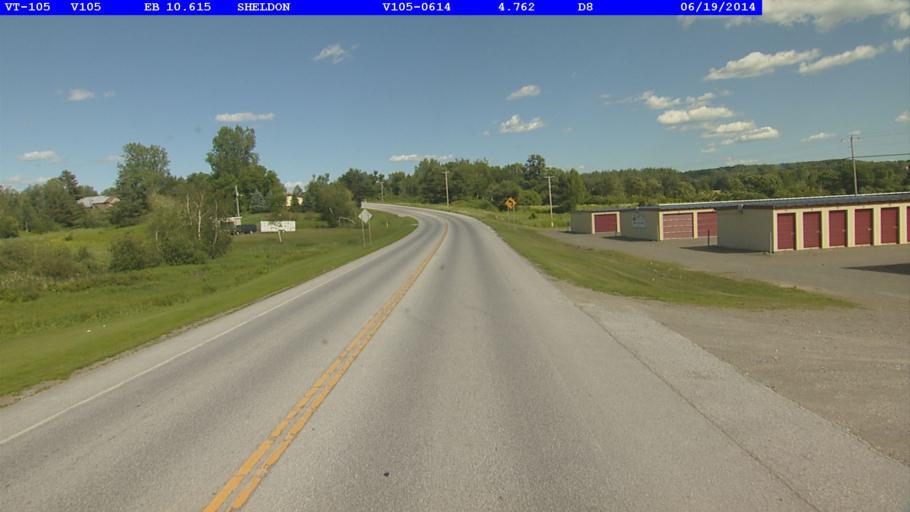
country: US
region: Vermont
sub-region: Franklin County
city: Enosburg Falls
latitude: 44.9013
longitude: -72.9397
